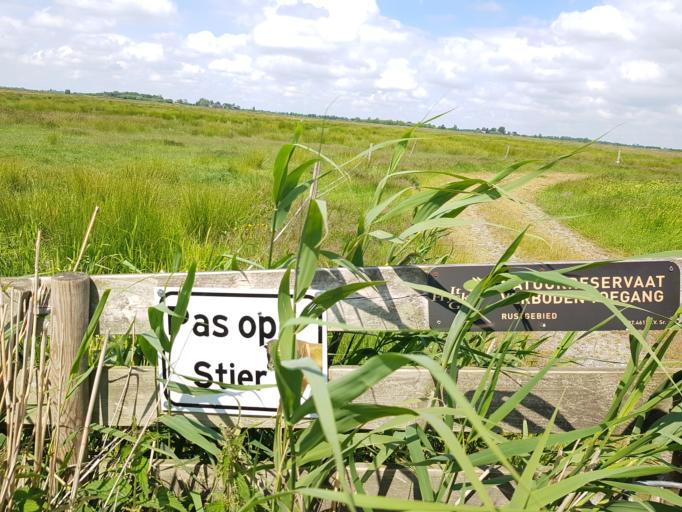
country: NL
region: Friesland
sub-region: Gemeente Boarnsterhim
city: Aldeboarn
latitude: 53.0936
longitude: 5.9080
